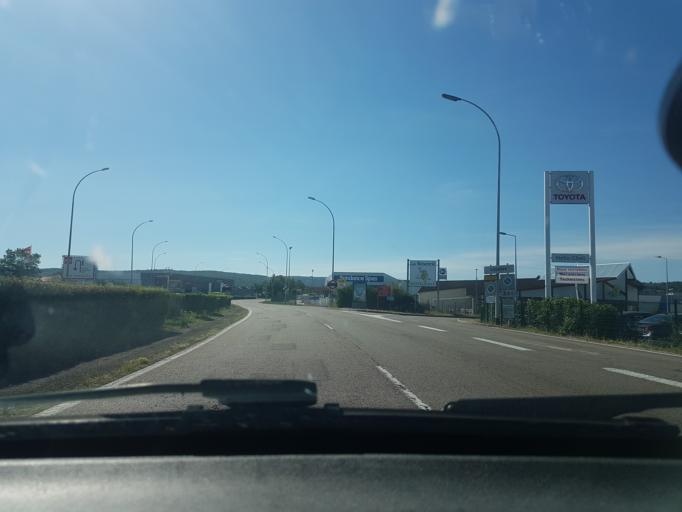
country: FR
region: Bourgogne
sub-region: Departement de la Cote-d'Or
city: Chenove
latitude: 47.2820
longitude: 5.0135
